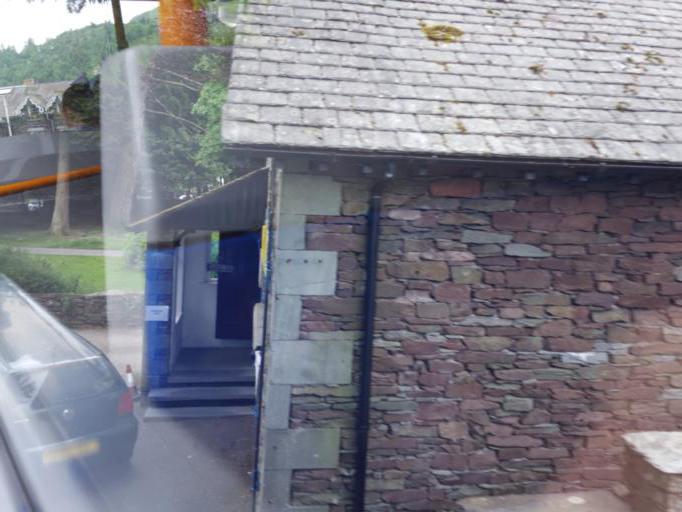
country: GB
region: England
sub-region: Cumbria
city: Ambleside
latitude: 54.4588
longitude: -3.0245
